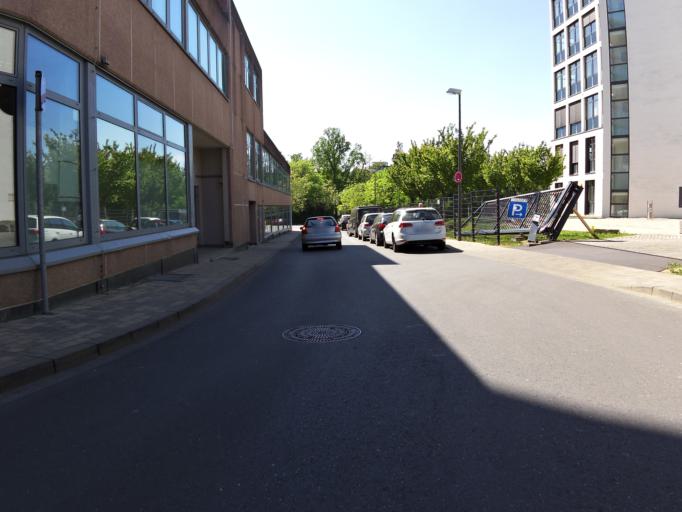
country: DE
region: Bavaria
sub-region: Regierungsbezirk Unterfranken
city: Wuerzburg
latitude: 49.7980
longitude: 9.9450
